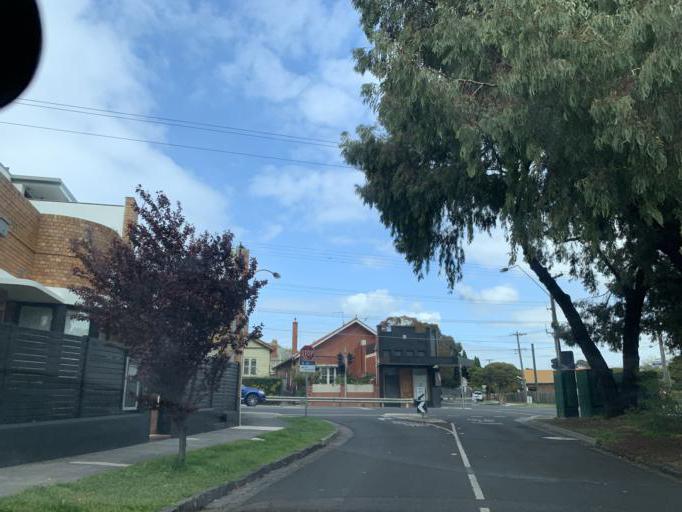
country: AU
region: Victoria
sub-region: Moreland
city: Coburg
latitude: -37.7540
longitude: 144.9542
